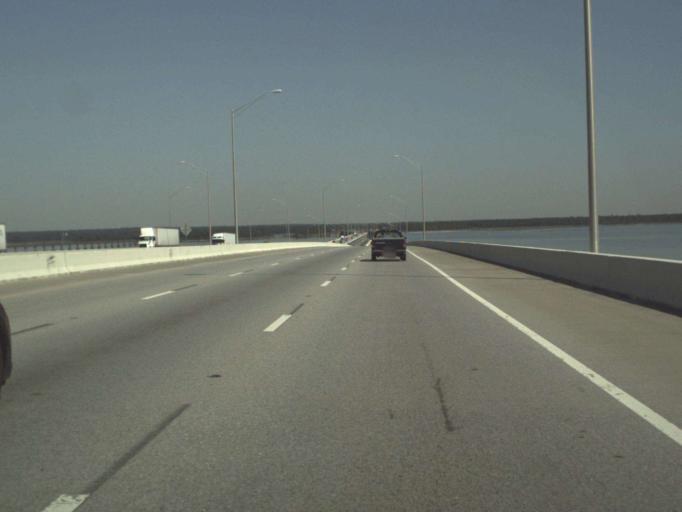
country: US
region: Florida
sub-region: Escambia County
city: Ferry Pass
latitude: 30.5171
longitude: -87.1464
